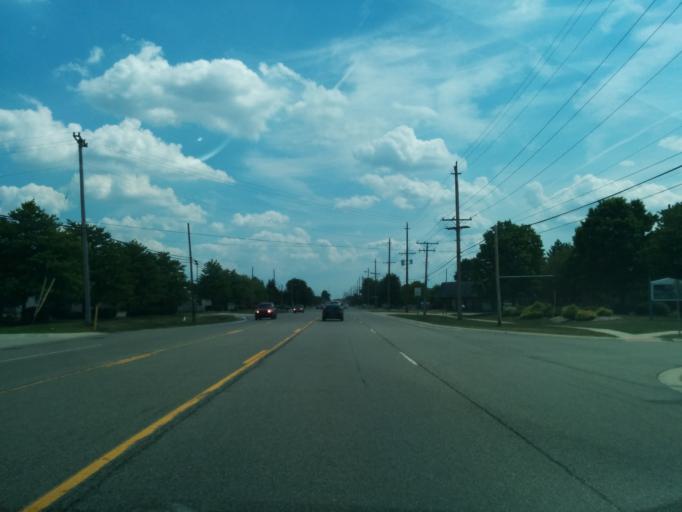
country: US
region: Michigan
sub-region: Oakland County
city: Novi
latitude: 42.4738
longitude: -83.4445
